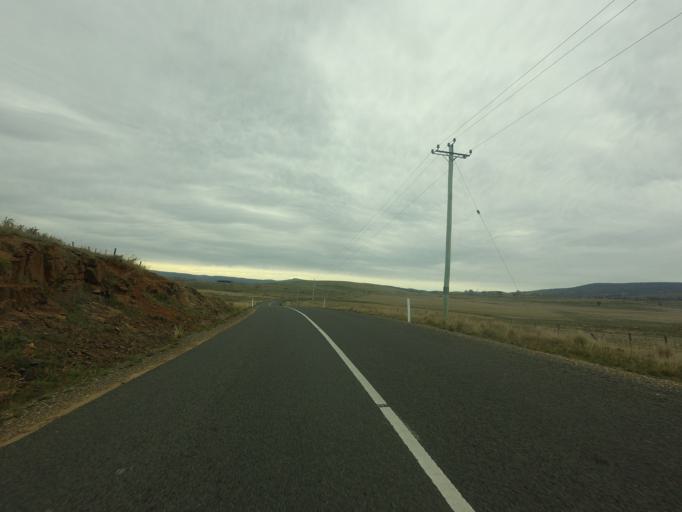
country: AU
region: Tasmania
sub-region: Derwent Valley
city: New Norfolk
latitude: -42.4323
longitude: 146.9858
